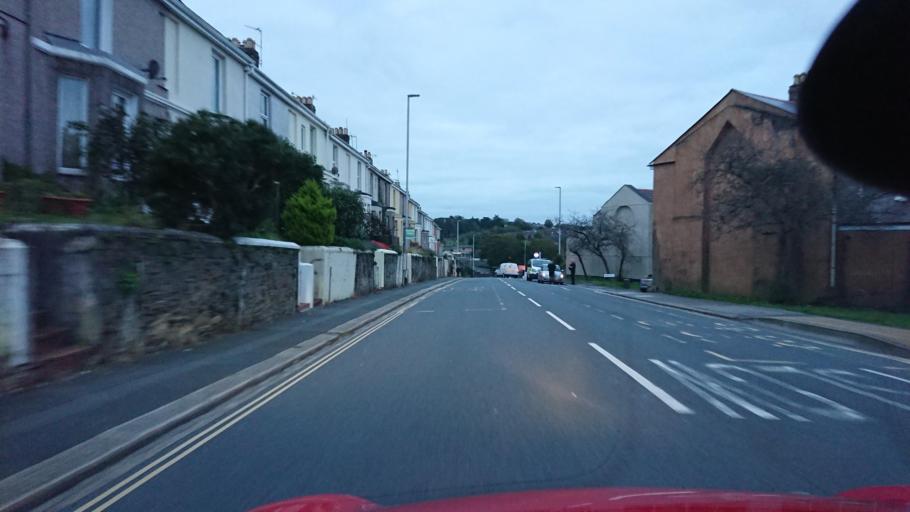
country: GB
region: England
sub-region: Cornwall
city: Torpoint
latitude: 50.3973
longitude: -4.1821
